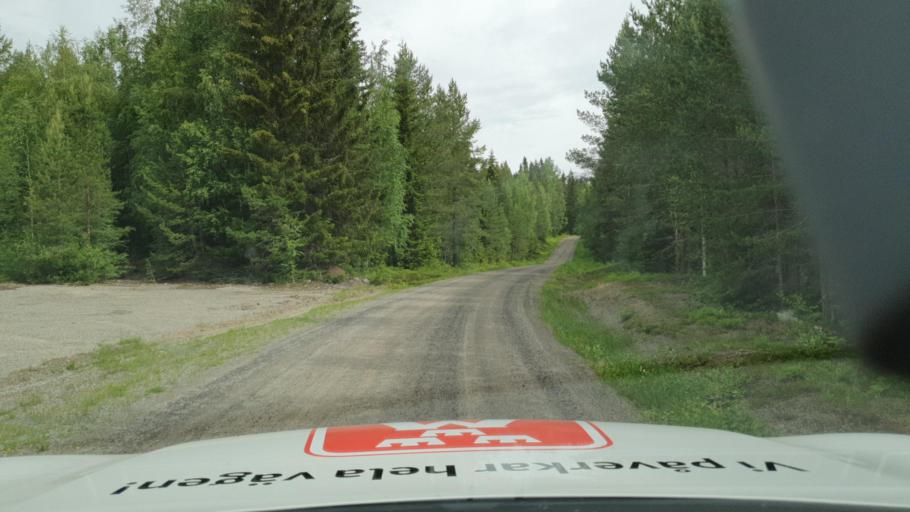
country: SE
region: Vaesterbotten
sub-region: Robertsfors Kommun
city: Robertsfors
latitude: 64.2630
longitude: 20.6639
